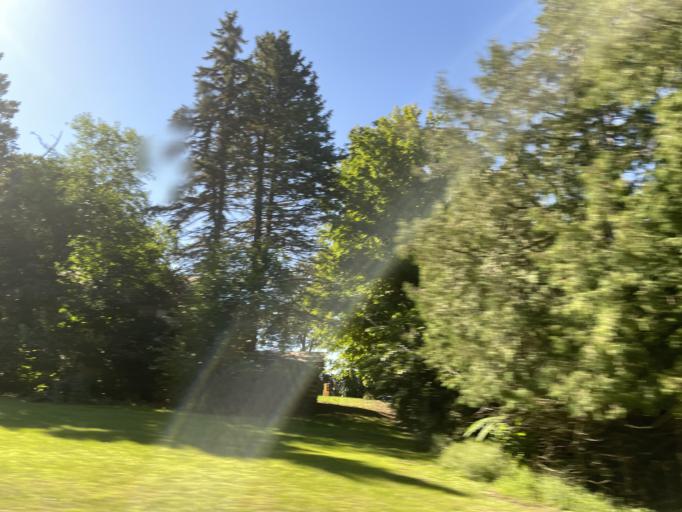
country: US
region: Michigan
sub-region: Benzie County
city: Beulah
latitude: 44.6174
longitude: -86.0765
